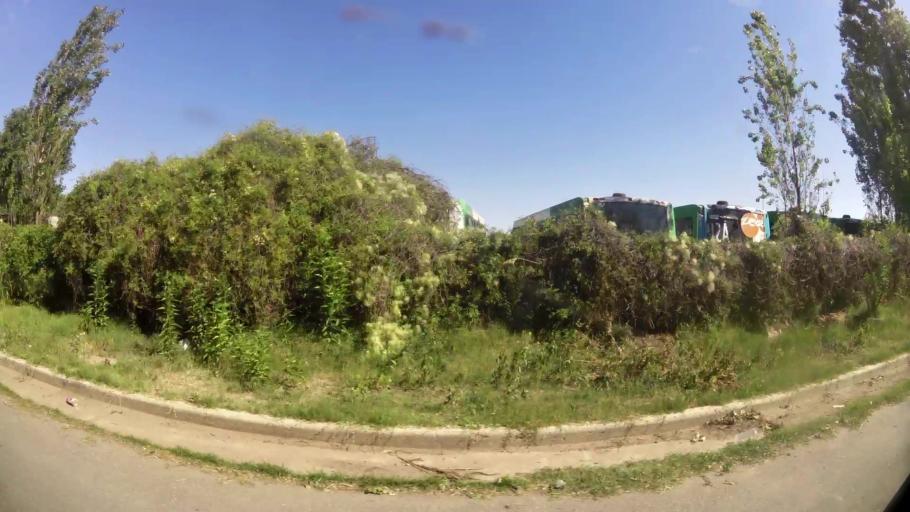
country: AR
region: Cordoba
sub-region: Departamento de Capital
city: Cordoba
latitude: -31.3650
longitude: -64.1538
